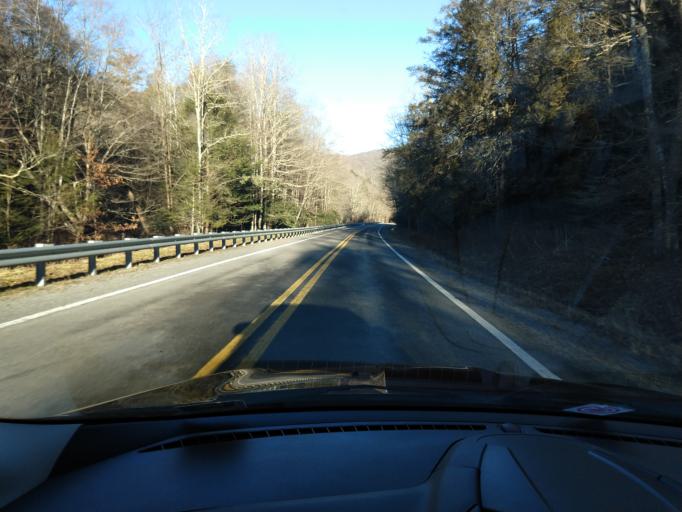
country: US
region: Virginia
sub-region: Highland County
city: Monterey
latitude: 38.5147
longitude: -79.7228
